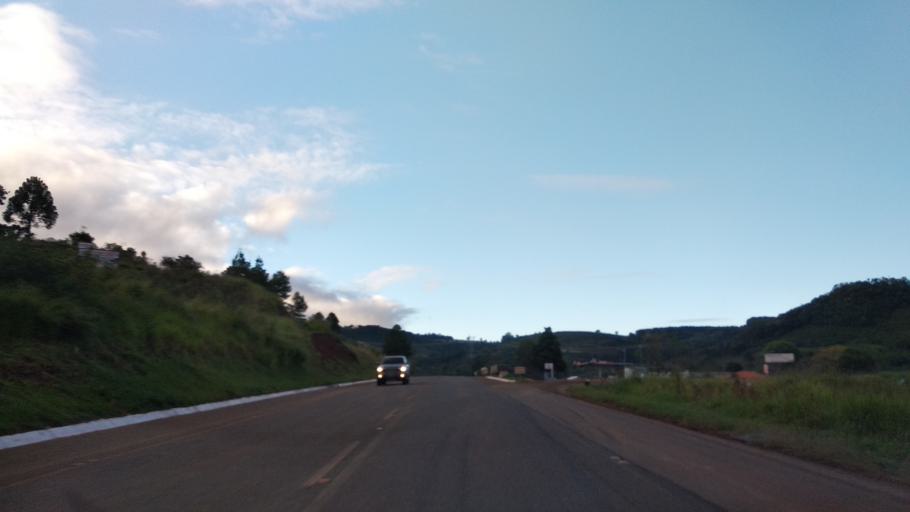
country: BR
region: Santa Catarina
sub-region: Curitibanos
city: Curitibanos
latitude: -27.5562
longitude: -50.8429
